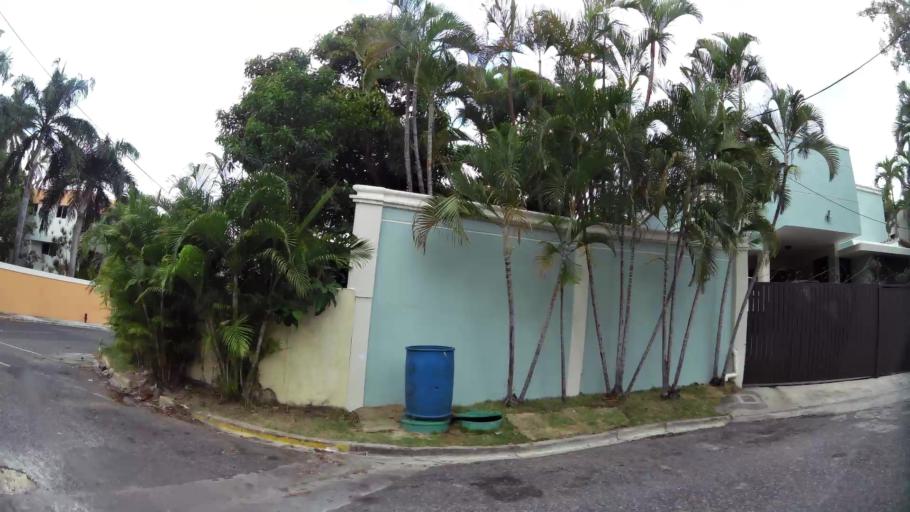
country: DO
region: Nacional
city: La Agustina
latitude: 18.4958
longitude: -69.9360
